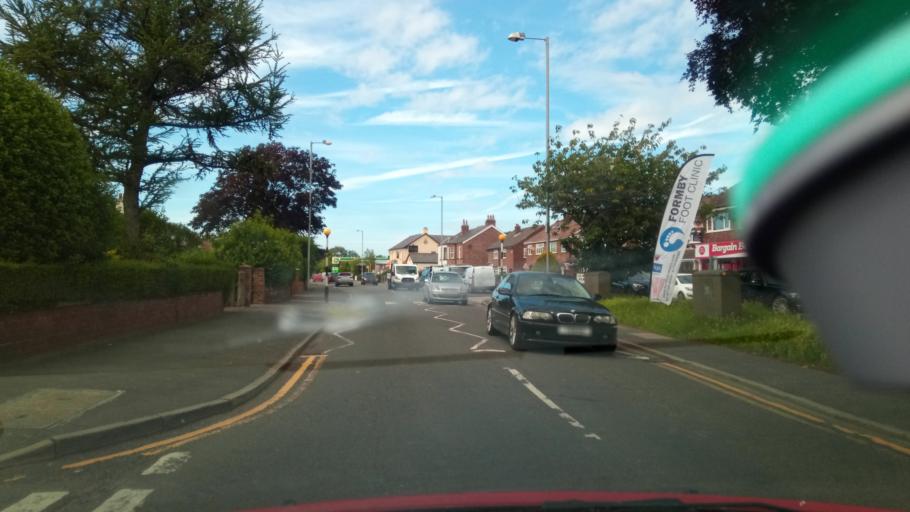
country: GB
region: England
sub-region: Sefton
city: Formby
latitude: 53.5481
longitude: -3.0545
